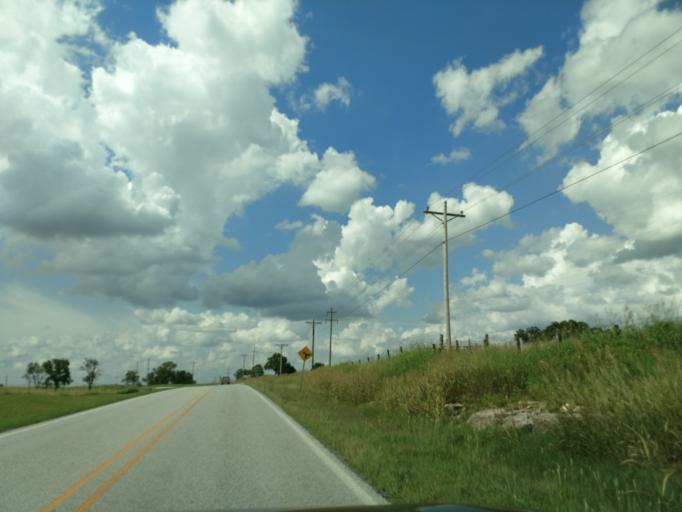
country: US
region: Arkansas
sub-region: Carroll County
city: Berryville
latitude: 36.4674
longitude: -93.5557
